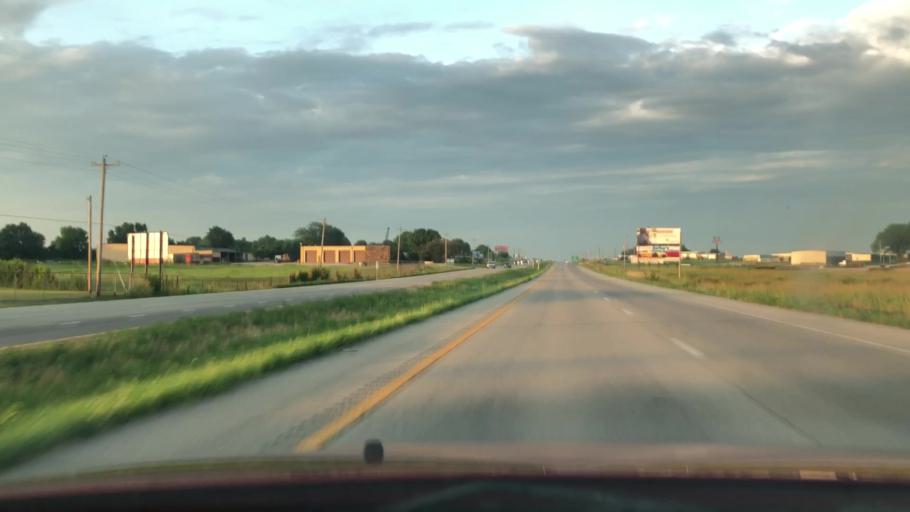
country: US
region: Missouri
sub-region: Greene County
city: Battlefield
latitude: 37.1550
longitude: -93.4112
